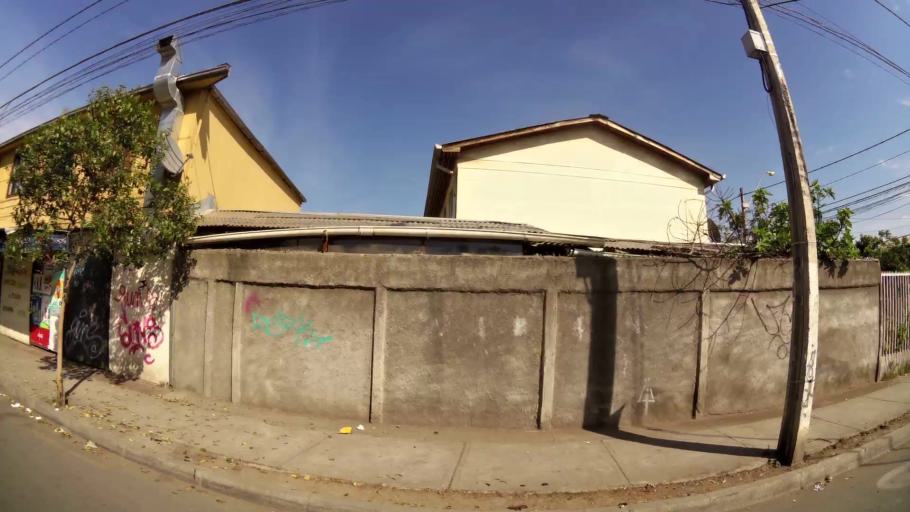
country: CL
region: Santiago Metropolitan
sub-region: Provincia de Santiago
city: La Pintana
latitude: -33.5635
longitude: -70.6333
